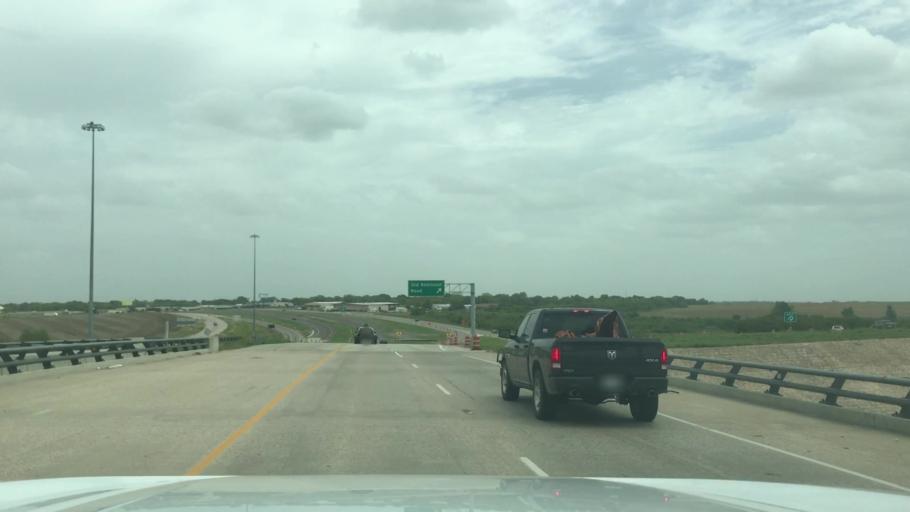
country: US
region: Texas
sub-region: McLennan County
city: Beverly Hills
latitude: 31.4930
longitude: -97.1508
